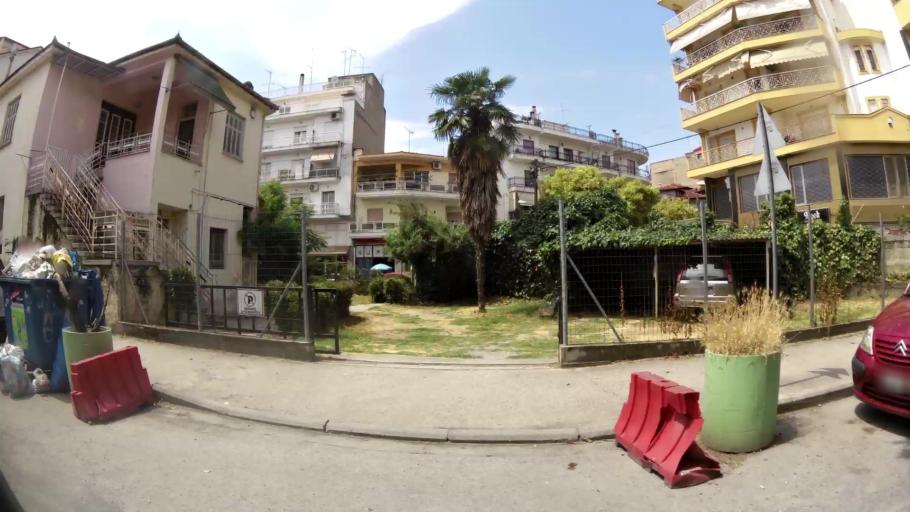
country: GR
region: Central Macedonia
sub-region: Nomos Pierias
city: Katerini
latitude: 40.2691
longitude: 22.5085
